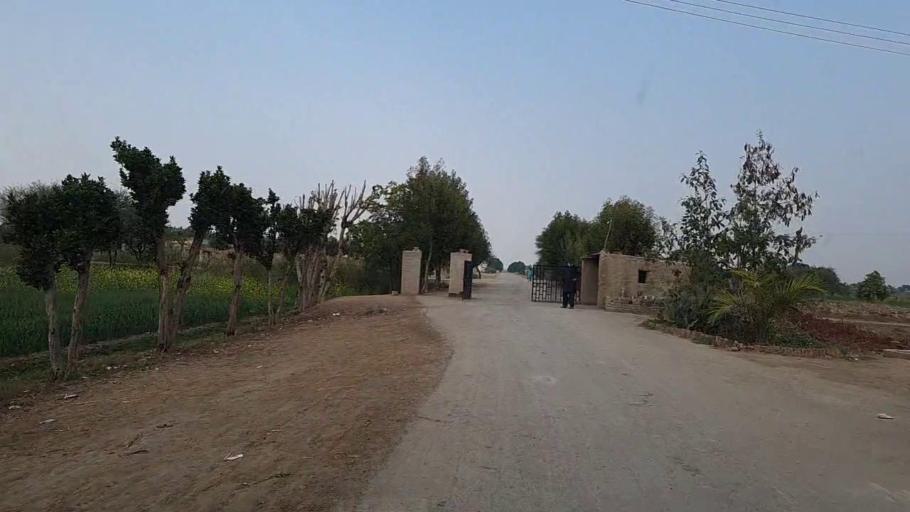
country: PK
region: Sindh
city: Mirwah Gorchani
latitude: 25.3710
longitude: 69.0817
